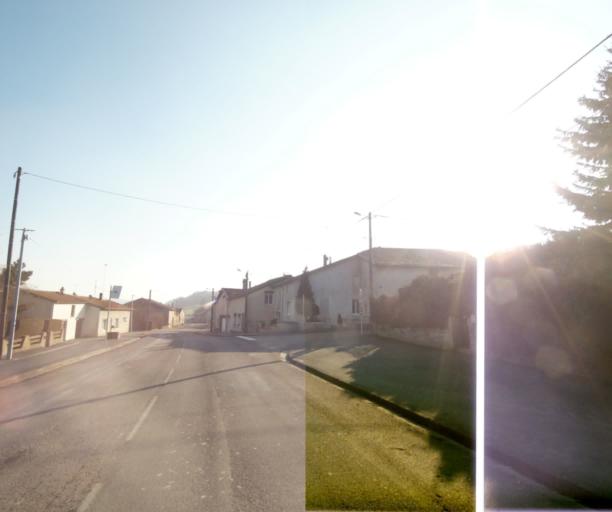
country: FR
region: Champagne-Ardenne
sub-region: Departement de la Haute-Marne
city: Chevillon
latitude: 48.5068
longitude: 5.1135
